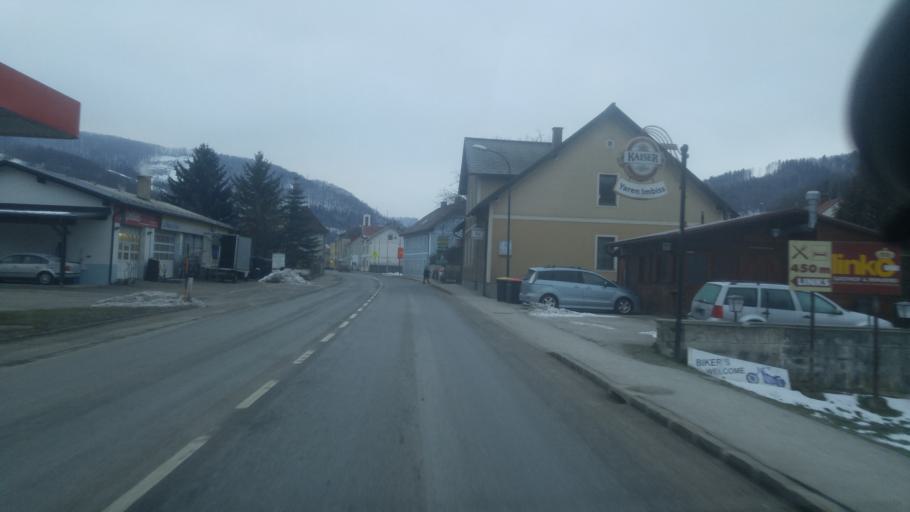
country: AT
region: Lower Austria
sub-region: Politischer Bezirk Lilienfeld
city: Traisen
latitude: 48.0450
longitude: 15.6090
